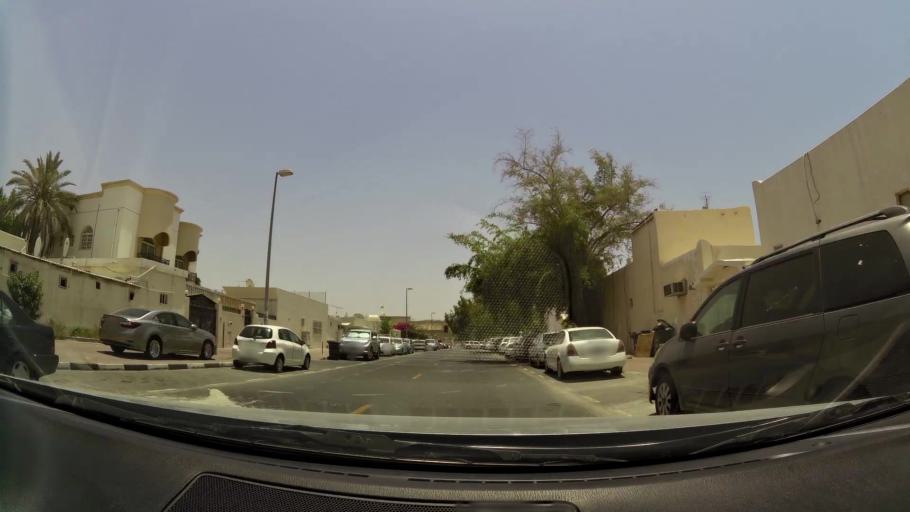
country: AE
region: Ash Shariqah
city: Sharjah
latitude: 25.2287
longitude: 55.2665
